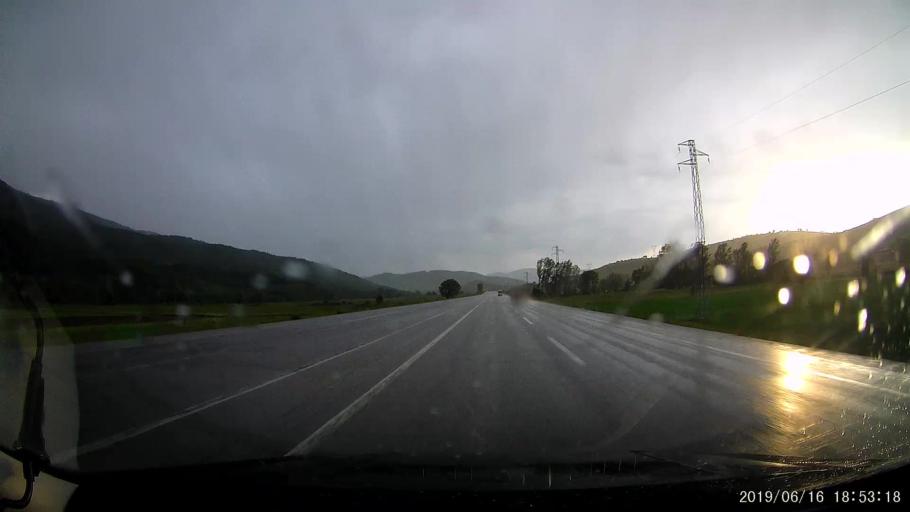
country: TR
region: Erzincan
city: Catalcam
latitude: 39.8990
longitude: 38.8807
